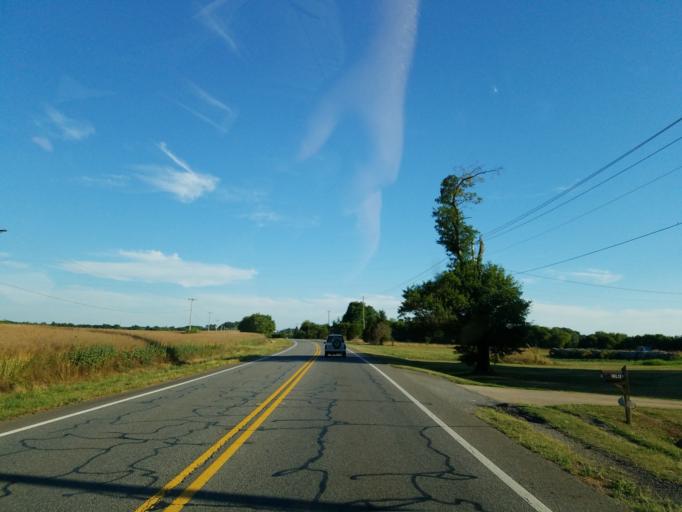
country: US
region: Georgia
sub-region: Bartow County
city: Adairsville
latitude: 34.4122
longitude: -84.9365
